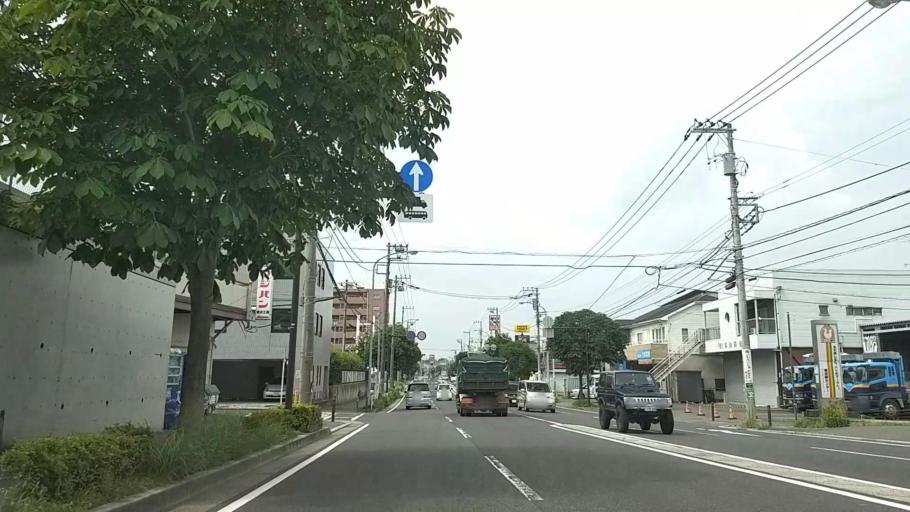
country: JP
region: Kanagawa
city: Minami-rinkan
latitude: 35.4989
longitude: 139.5392
